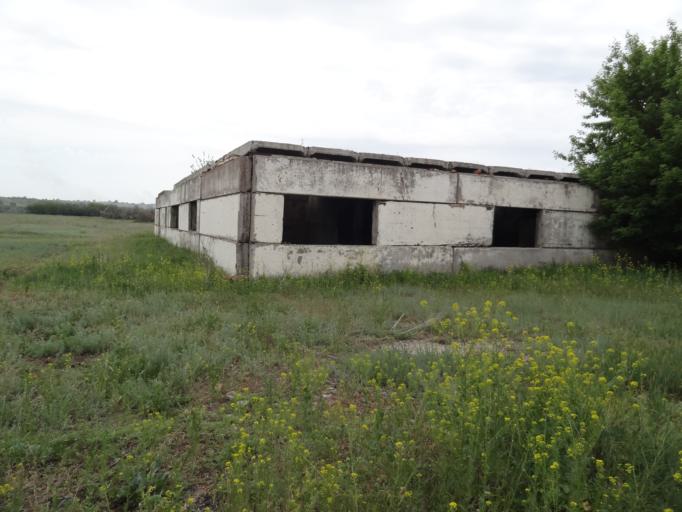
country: RU
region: Saratov
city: Krasnoarmeysk
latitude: 51.1689
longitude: 45.9111
